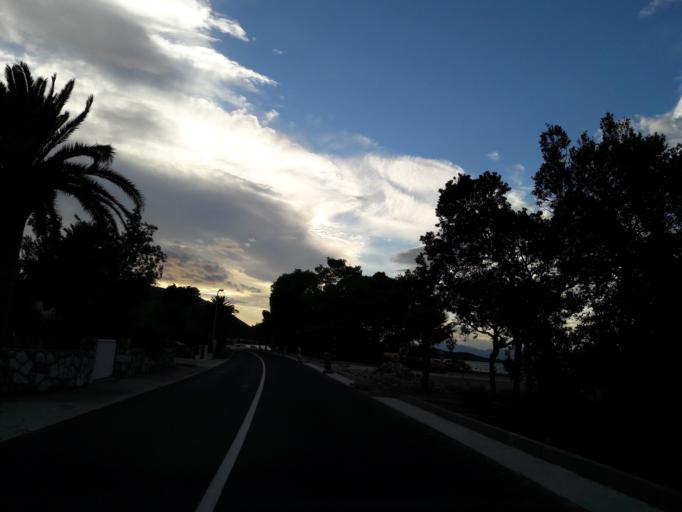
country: HR
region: Dubrovacko-Neretvanska
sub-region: Grad Dubrovnik
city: Opuzen
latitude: 42.9202
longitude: 17.4645
